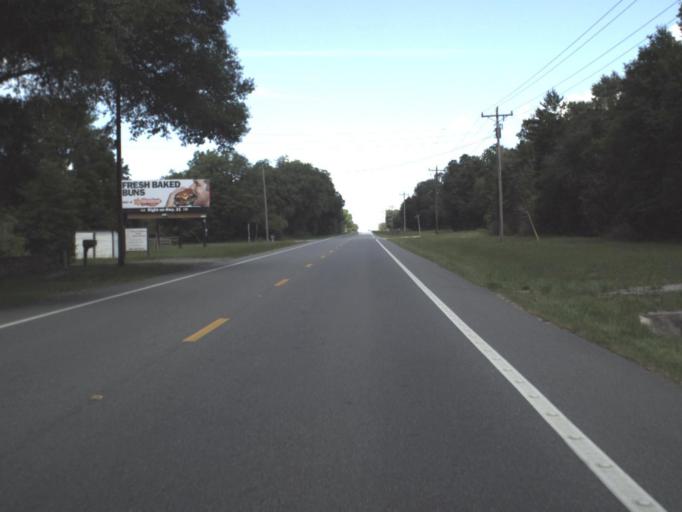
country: US
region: Florida
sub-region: Clay County
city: Keystone Heights
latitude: 29.7410
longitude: -81.9699
